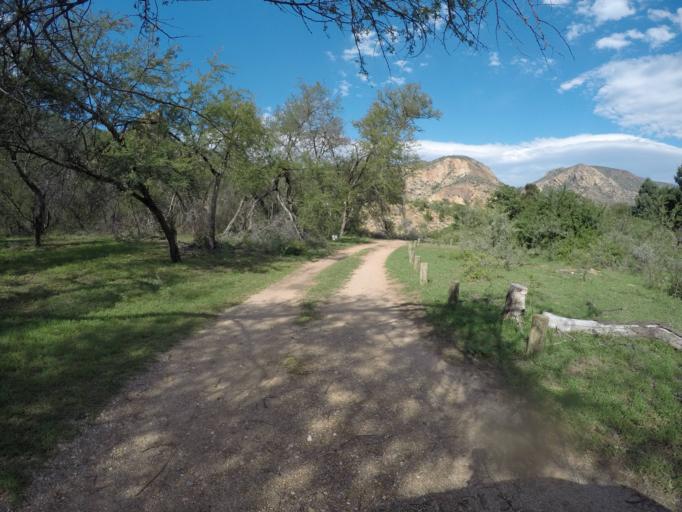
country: ZA
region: Eastern Cape
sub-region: Cacadu District Municipality
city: Kareedouw
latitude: -33.6583
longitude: 24.4322
